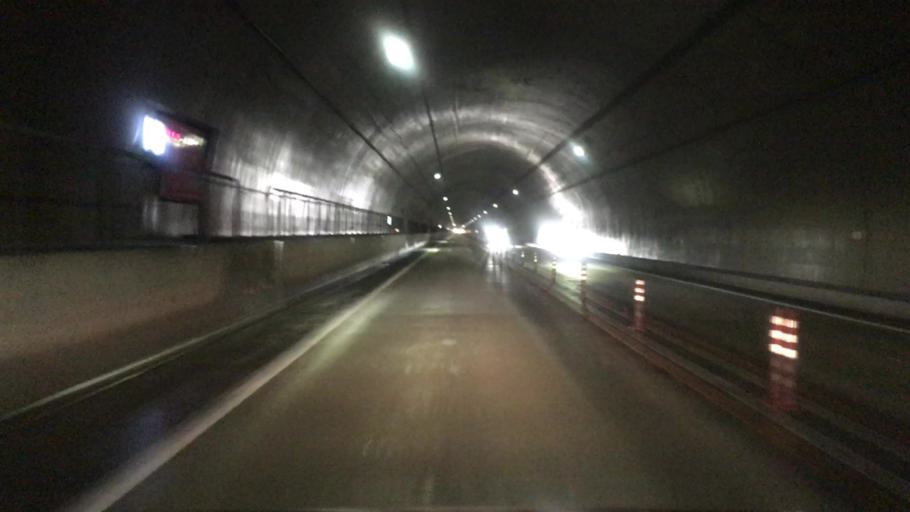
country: JP
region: Hyogo
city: Toyooka
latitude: 35.6391
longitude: 134.5431
